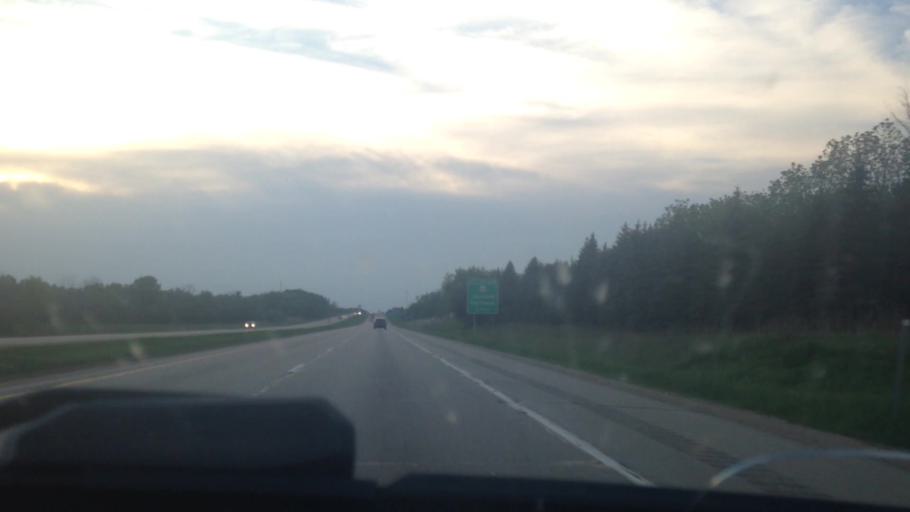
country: US
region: Wisconsin
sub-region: Washington County
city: Slinger
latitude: 43.3108
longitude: -88.2316
